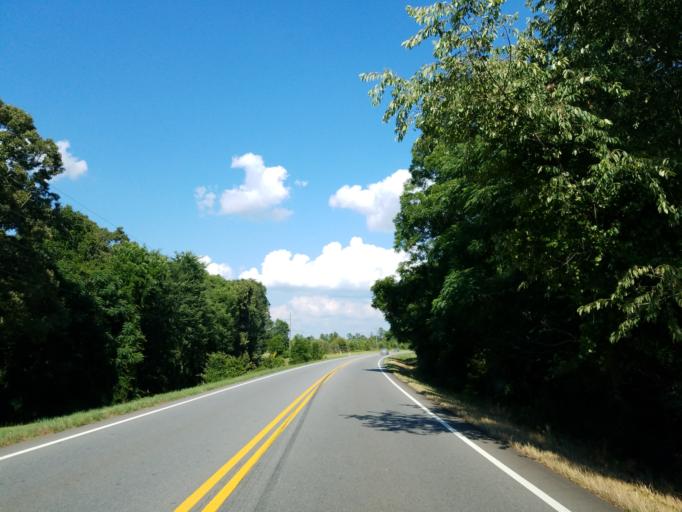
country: US
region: Georgia
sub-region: Peach County
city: Byron
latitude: 32.5537
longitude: -83.7804
